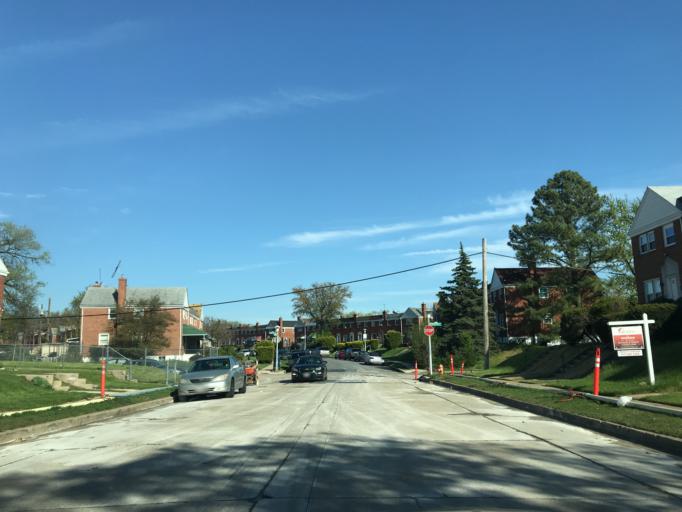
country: US
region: Maryland
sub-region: Baltimore County
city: Rosedale
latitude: 39.3235
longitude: -76.5578
